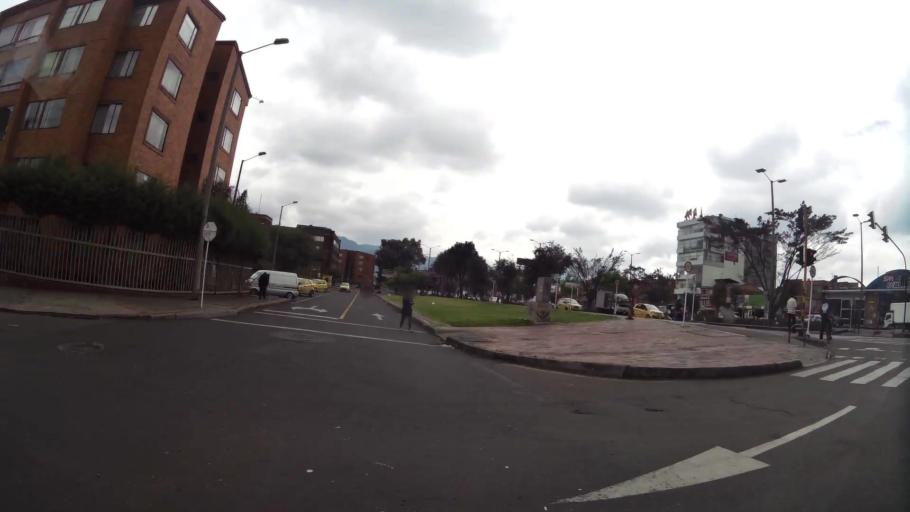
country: CO
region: Bogota D.C.
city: Barrio San Luis
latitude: 4.6889
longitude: -74.0820
